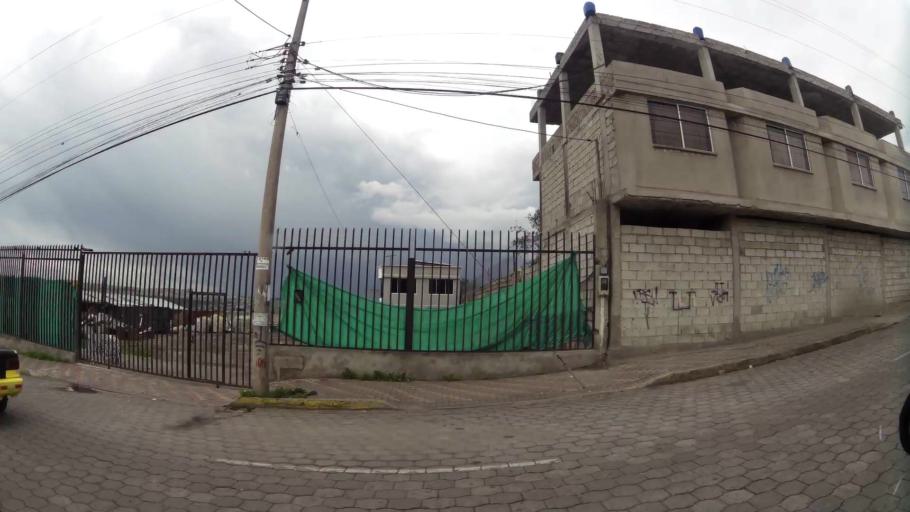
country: EC
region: Pichincha
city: Sangolqui
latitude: -0.3305
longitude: -78.5532
